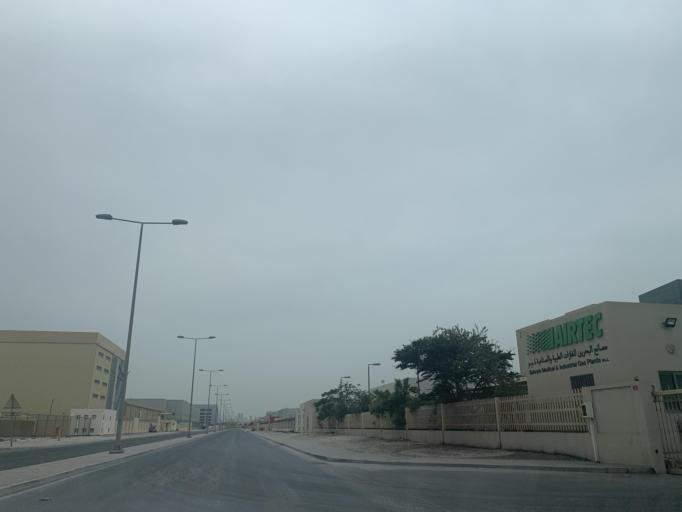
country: BH
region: Muharraq
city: Al Hadd
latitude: 26.2150
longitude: 50.6785
